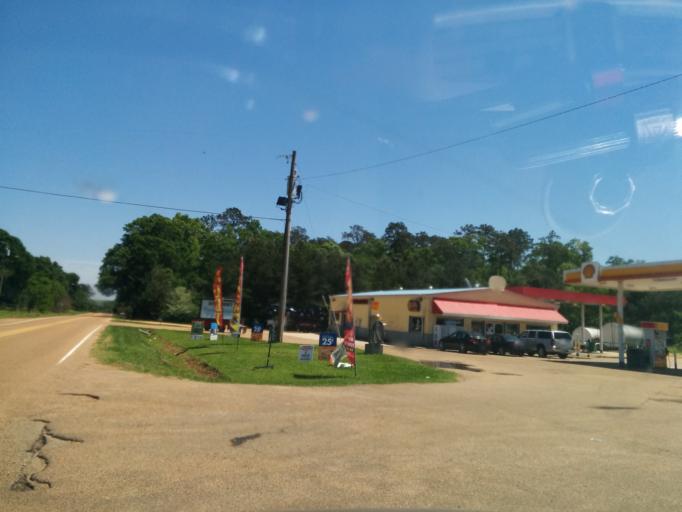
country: US
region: Mississippi
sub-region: Pike County
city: Magnolia
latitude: 31.1458
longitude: -90.4768
